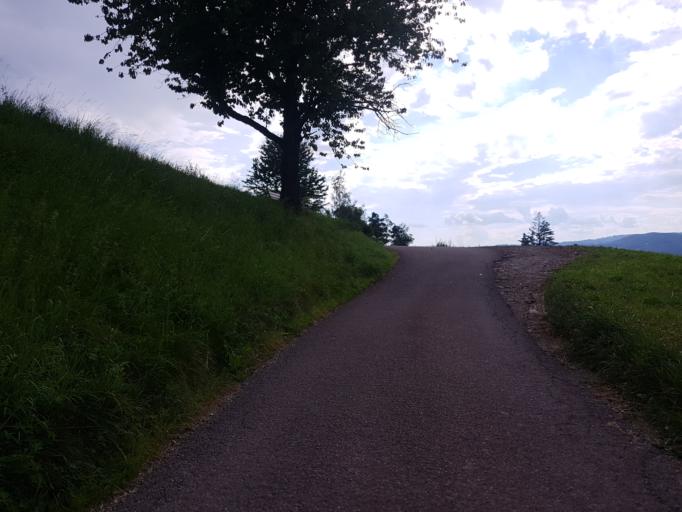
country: IT
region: Trentino-Alto Adige
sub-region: Bolzano
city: Siusi
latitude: 46.5421
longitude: 11.5520
